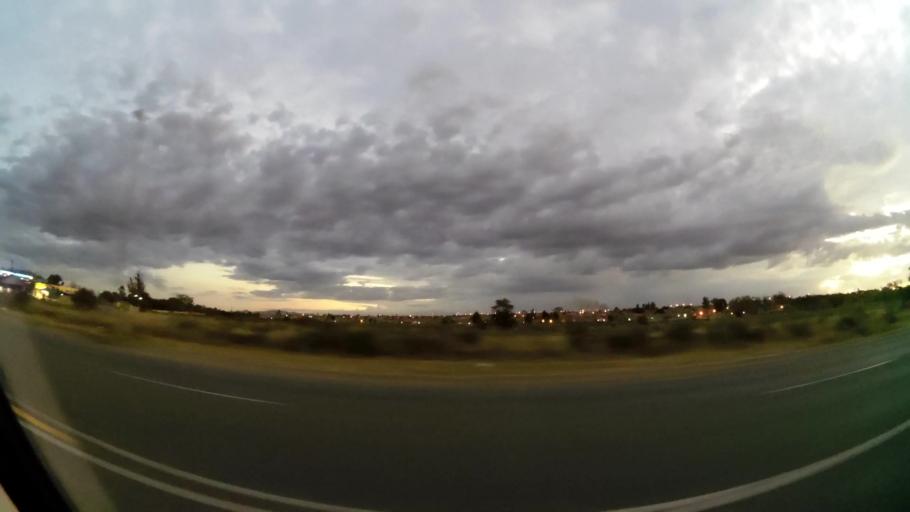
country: ZA
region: Limpopo
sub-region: Capricorn District Municipality
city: Polokwane
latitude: -23.8677
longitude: 29.4349
